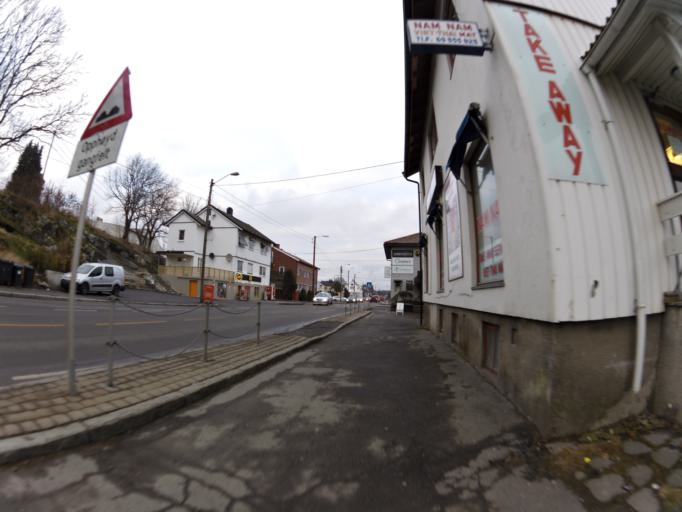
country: NO
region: Ostfold
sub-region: Fredrikstad
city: Fredrikstad
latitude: 59.2171
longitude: 10.9057
